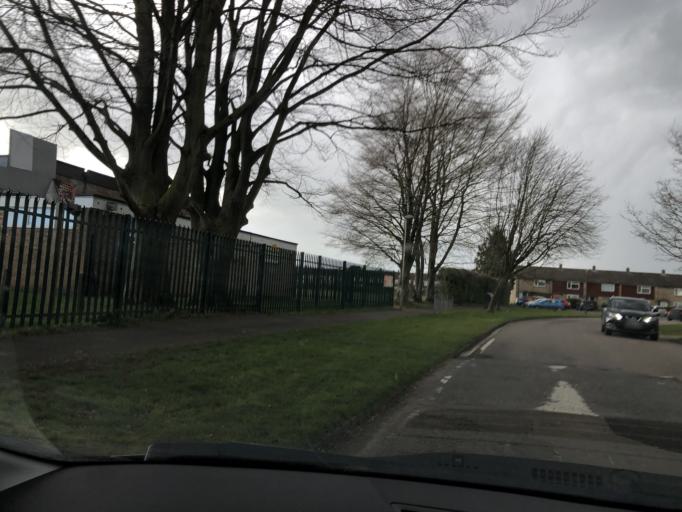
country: GB
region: England
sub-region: Oxfordshire
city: Bicester
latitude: 51.9002
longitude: -1.1665
